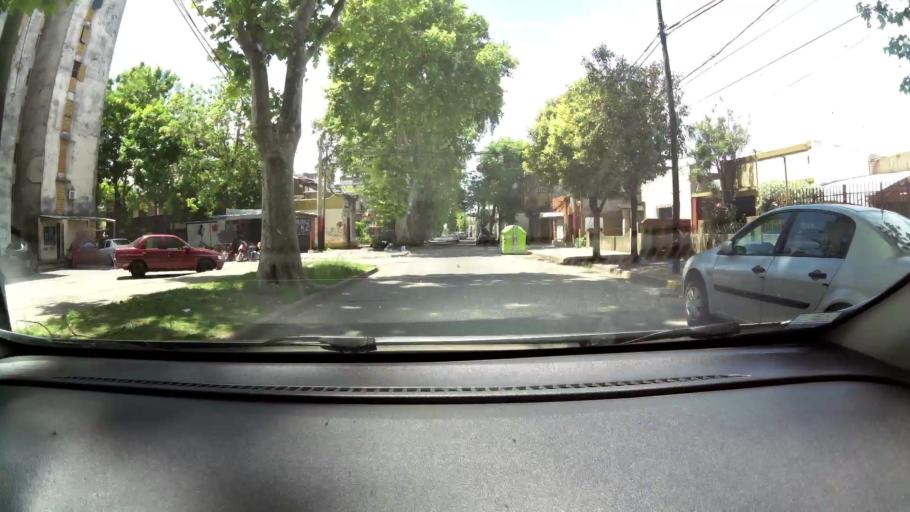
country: AR
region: Santa Fe
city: Gobernador Galvez
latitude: -32.9965
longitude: -60.6283
